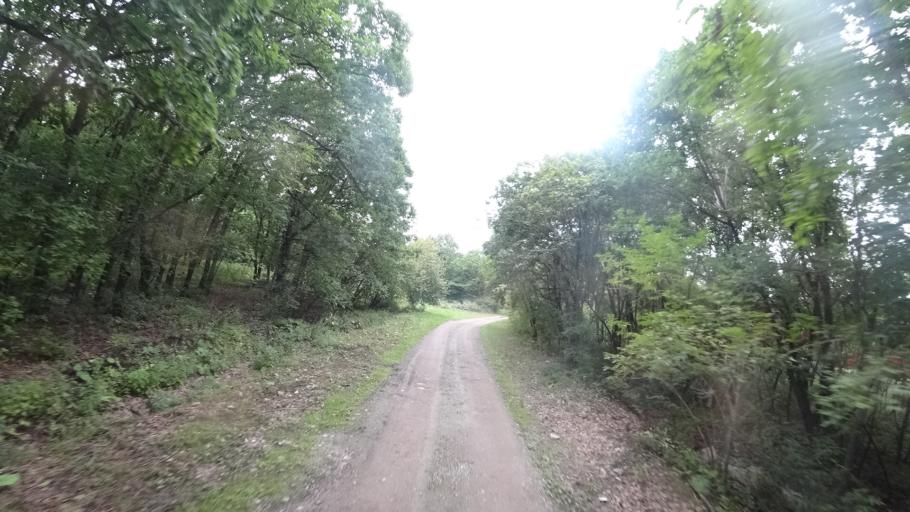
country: RU
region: Primorskiy
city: Monastyrishche
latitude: 44.2685
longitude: 132.4557
